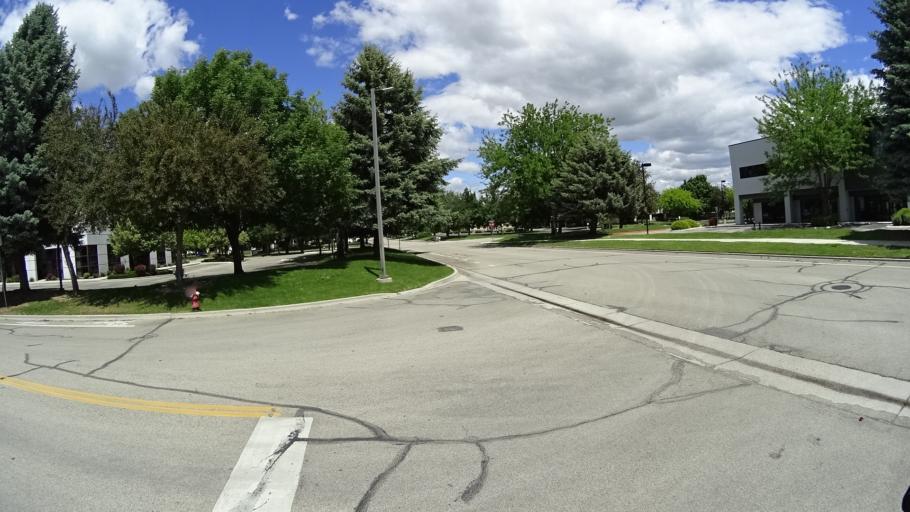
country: US
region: Idaho
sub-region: Ada County
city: Eagle
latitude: 43.6588
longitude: -116.3367
